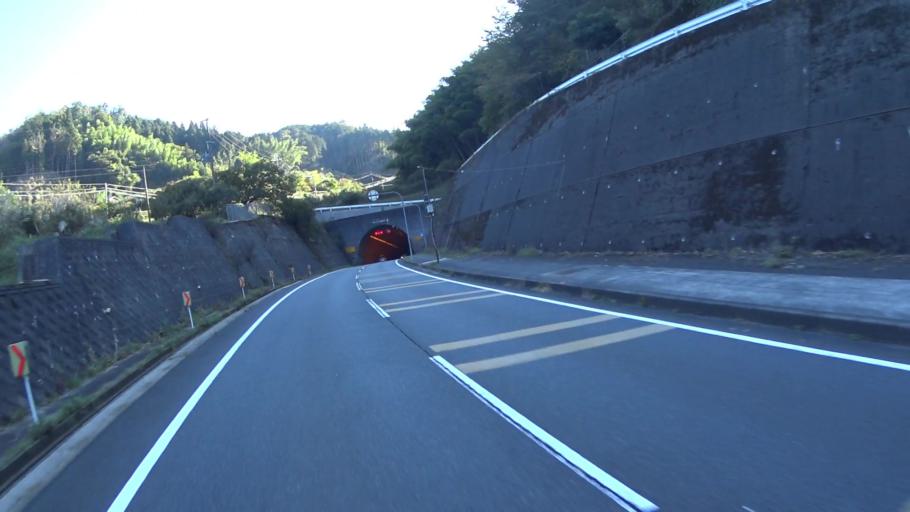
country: JP
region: Kyoto
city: Fukuchiyama
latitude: 35.4145
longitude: 135.0867
